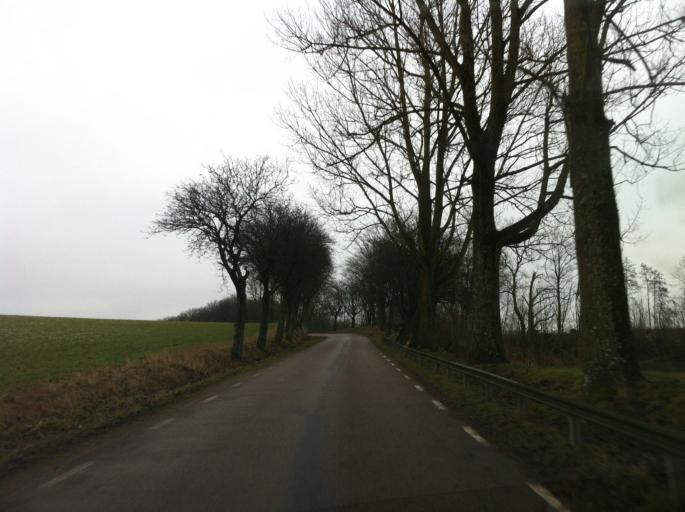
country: SE
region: Skane
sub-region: Landskrona
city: Asmundtorp
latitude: 55.9196
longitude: 12.9994
